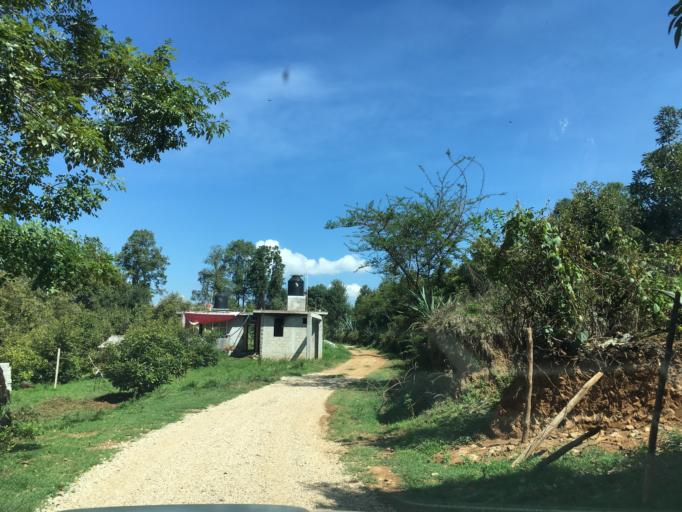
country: MX
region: Michoacan
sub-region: Zitacuaro
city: La Fundicion (Quinta Manzana)
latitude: 19.4893
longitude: -100.3144
